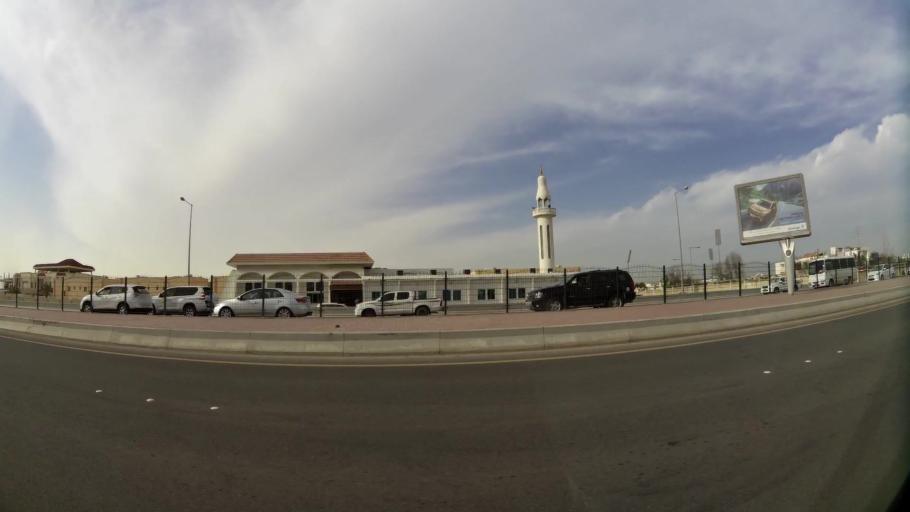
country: QA
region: Baladiyat ad Dawhah
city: Doha
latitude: 25.2543
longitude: 51.5170
